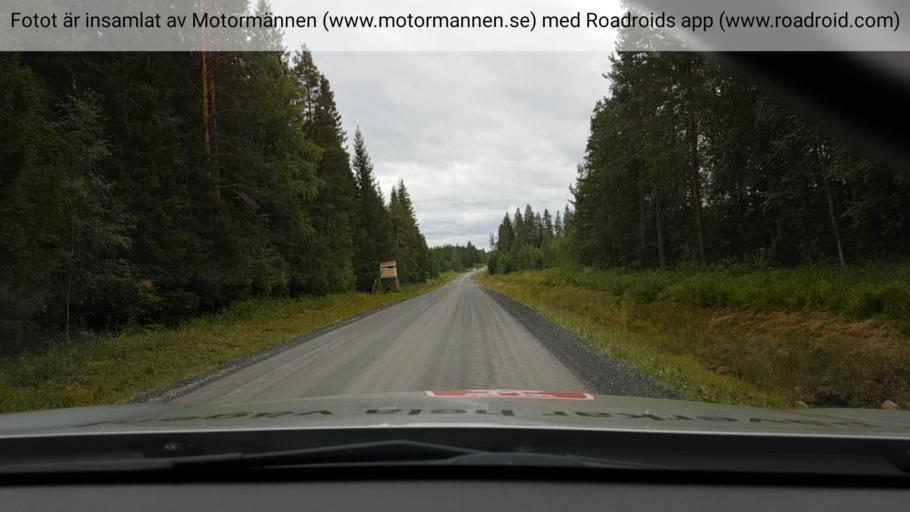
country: SE
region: Vaesterbotten
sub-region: Skelleftea Kommun
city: Forsbacka
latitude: 64.8248
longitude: 20.4972
